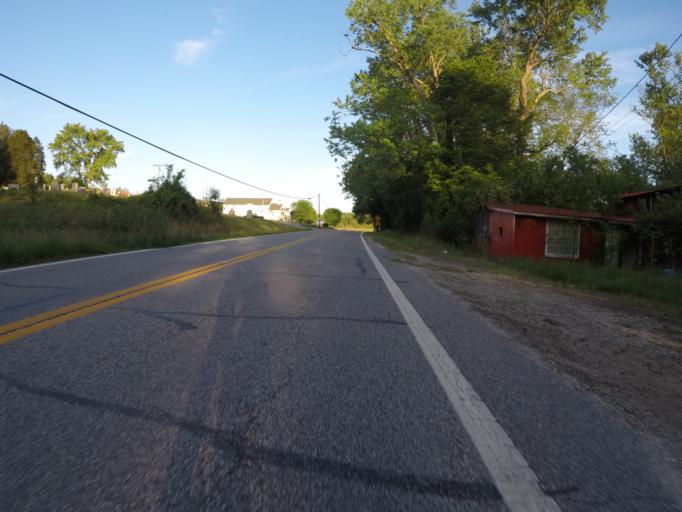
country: US
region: West Virginia
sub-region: Cabell County
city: Huntington
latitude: 38.4873
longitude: -82.4705
